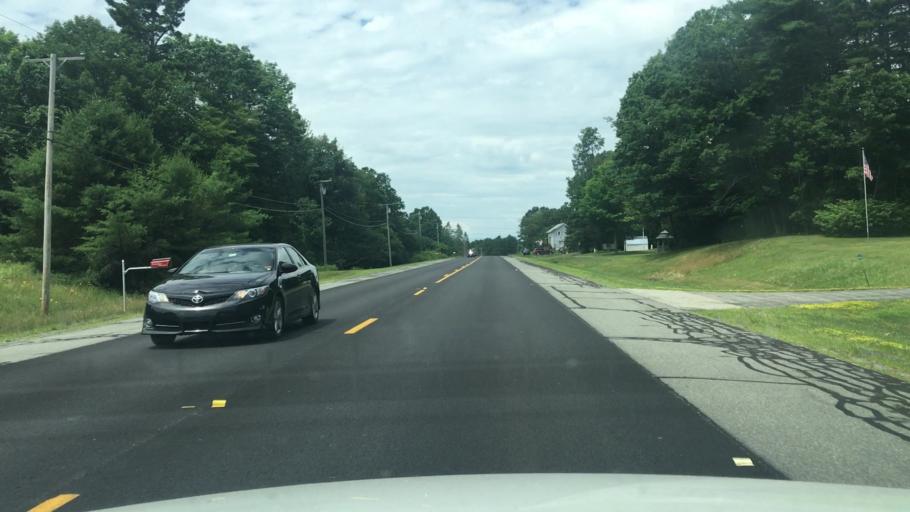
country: US
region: Maine
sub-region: Waldo County
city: Palermo
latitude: 44.3800
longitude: -69.4551
